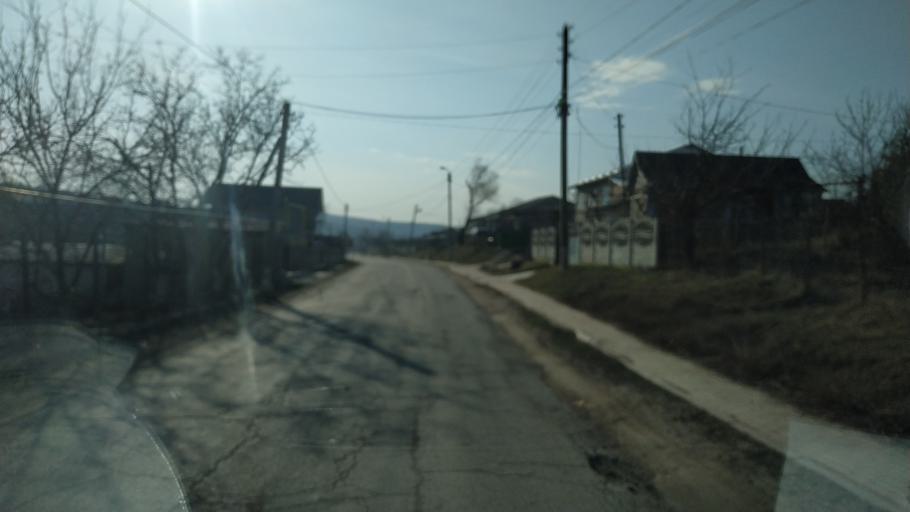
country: MD
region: Chisinau
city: Singera
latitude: 46.8296
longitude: 29.0333
